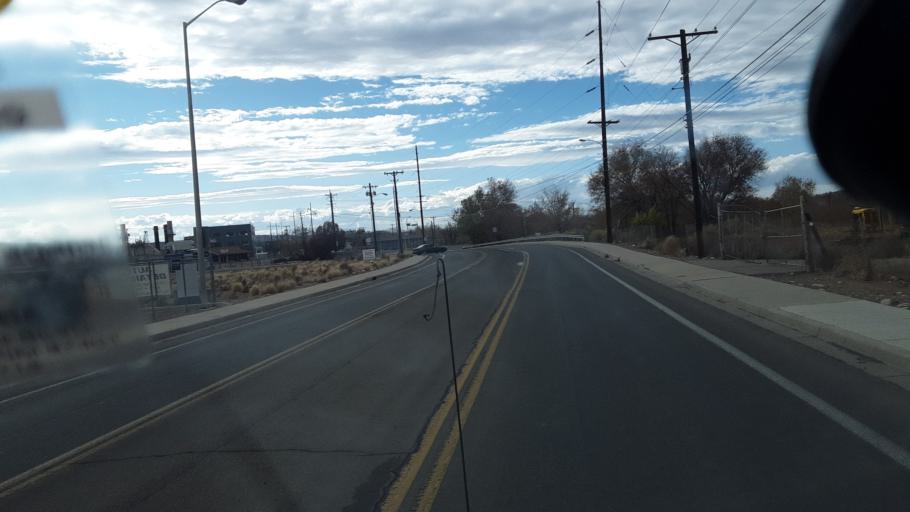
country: US
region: New Mexico
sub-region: San Juan County
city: Farmington
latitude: 36.7266
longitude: -108.1878
